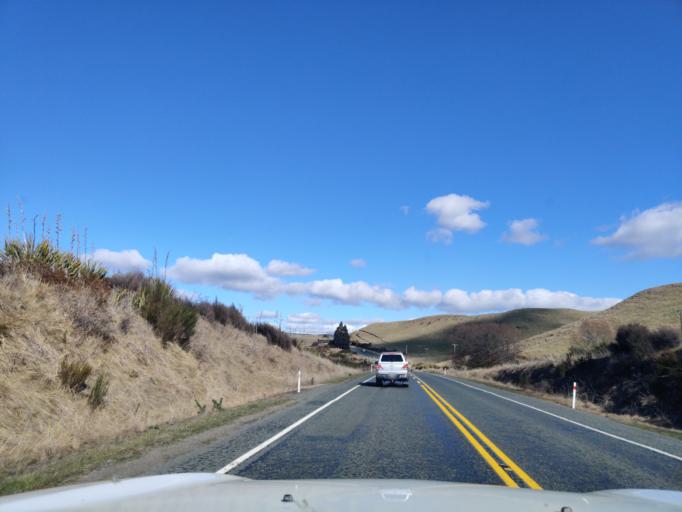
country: NZ
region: Manawatu-Wanganui
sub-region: Ruapehu District
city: Waiouru
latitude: -39.5207
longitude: 175.6853
